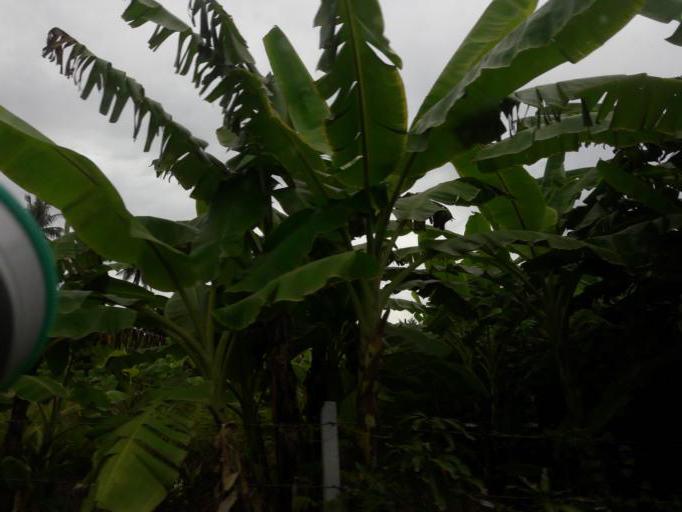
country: TH
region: Ratchaburi
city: Damnoen Saduak
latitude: 13.5119
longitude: 100.0224
